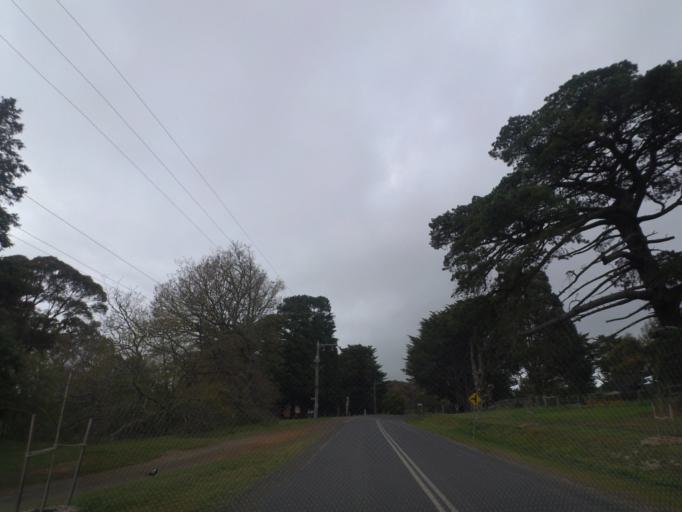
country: AU
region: Victoria
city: Brown Hill
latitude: -37.6295
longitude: 144.1054
